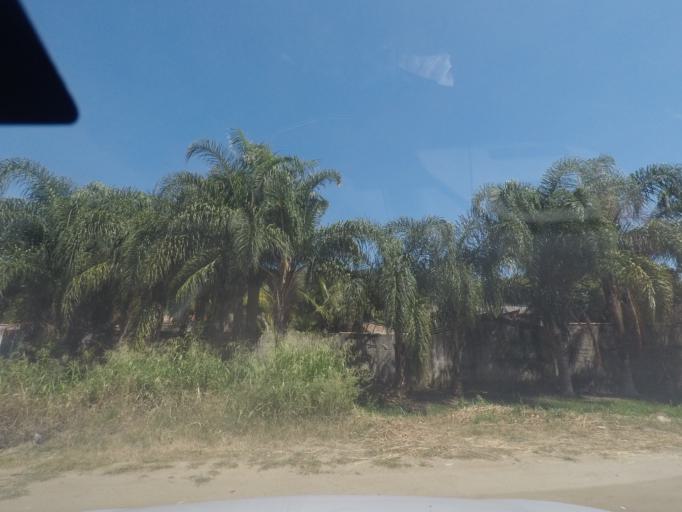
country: BR
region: Rio de Janeiro
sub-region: Niteroi
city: Niteroi
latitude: -22.9475
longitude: -43.0258
